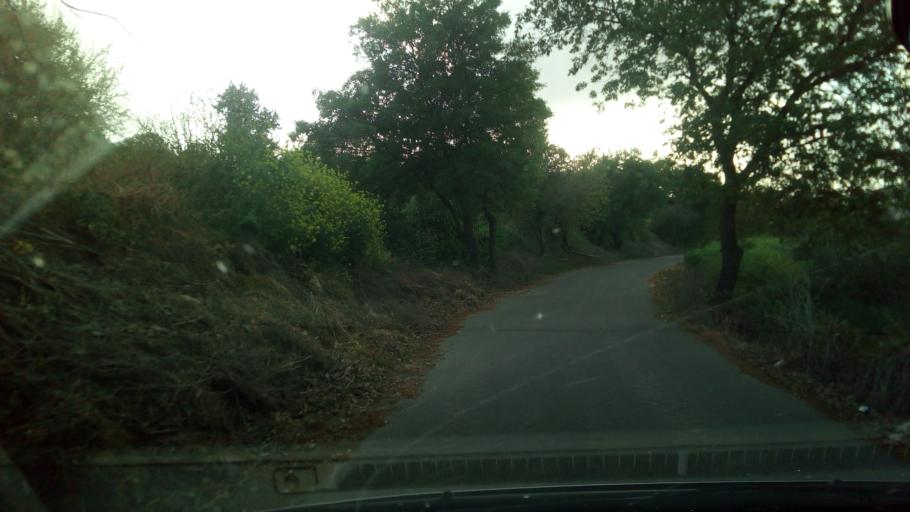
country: CY
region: Pafos
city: Polis
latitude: 34.9975
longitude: 32.5123
